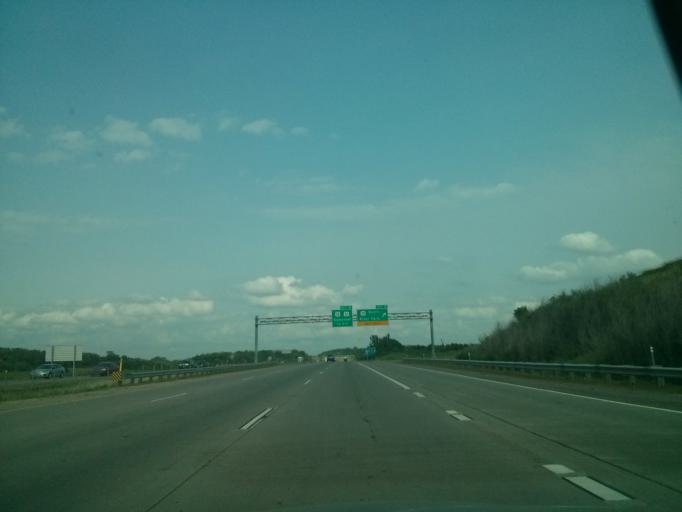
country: US
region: Wisconsin
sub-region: Saint Croix County
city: Hudson
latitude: 44.9637
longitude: -92.7016
